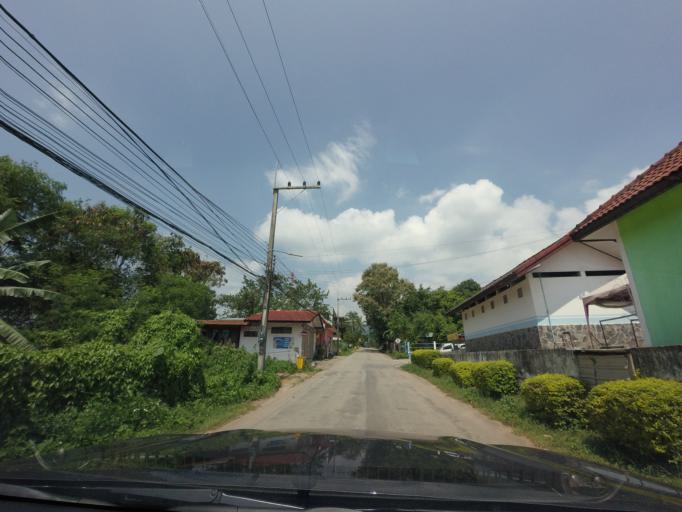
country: TH
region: Loei
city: Phu Ruea
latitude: 17.4539
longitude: 101.3621
